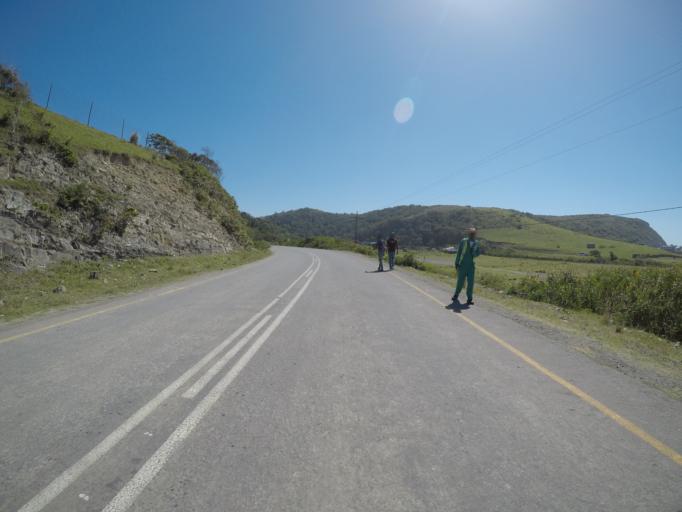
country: ZA
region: Eastern Cape
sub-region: OR Tambo District Municipality
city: Libode
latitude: -31.9816
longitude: 29.1478
